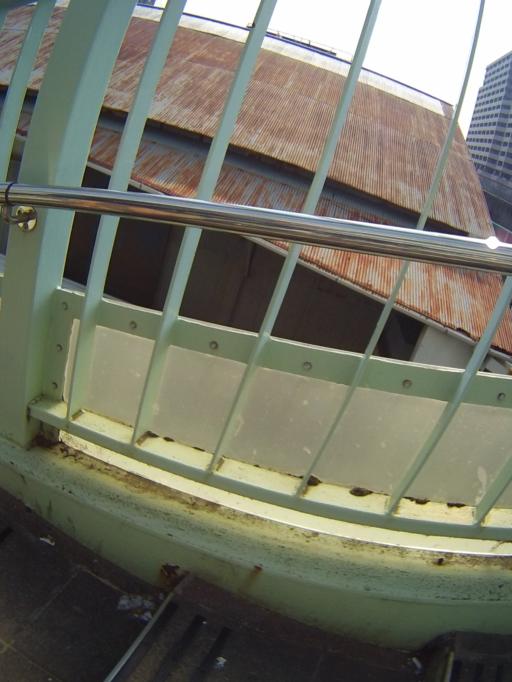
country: JP
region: Hyogo
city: Amagasaki
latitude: 34.6854
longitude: 135.4523
